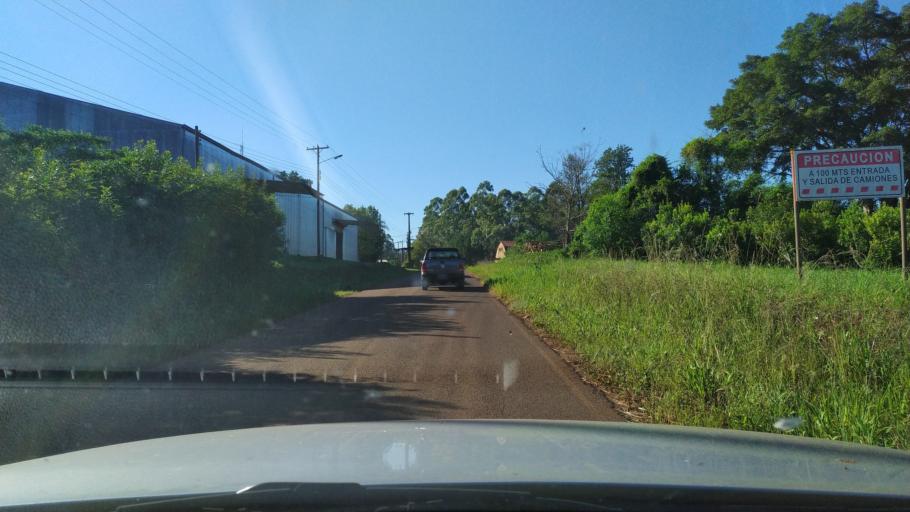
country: AR
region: Misiones
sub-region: Departamento de Montecarlo
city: Montecarlo
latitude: -26.6049
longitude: -54.7014
